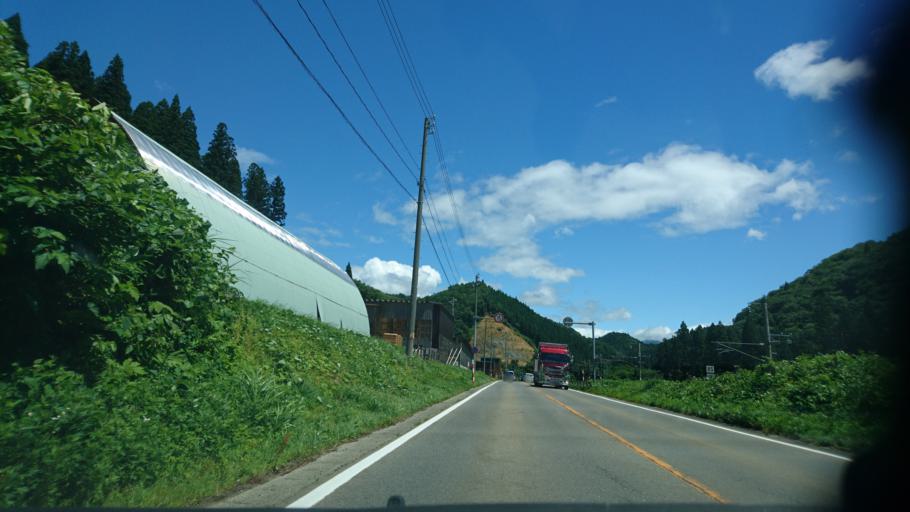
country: JP
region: Akita
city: Kakunodatemachi
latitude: 39.6487
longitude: 140.6658
